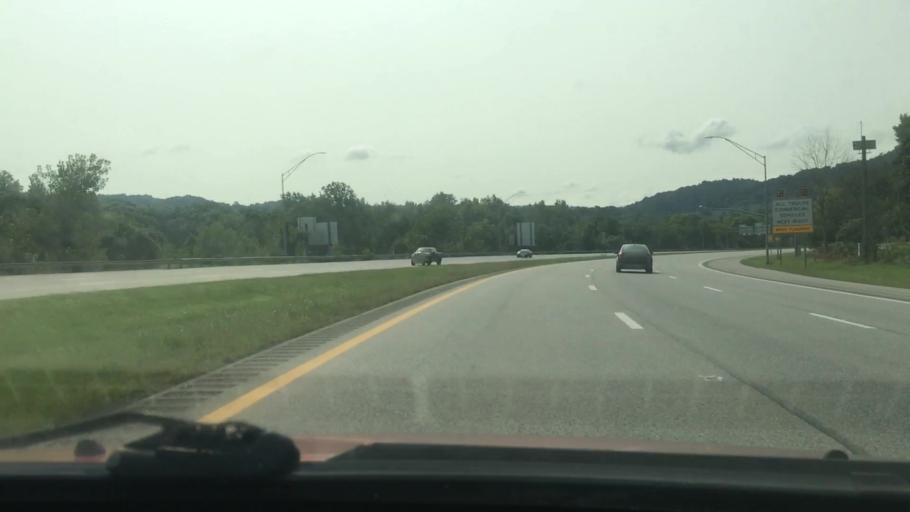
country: US
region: West Virginia
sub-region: Ohio County
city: Bethlehem
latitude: 40.0653
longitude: -80.6861
